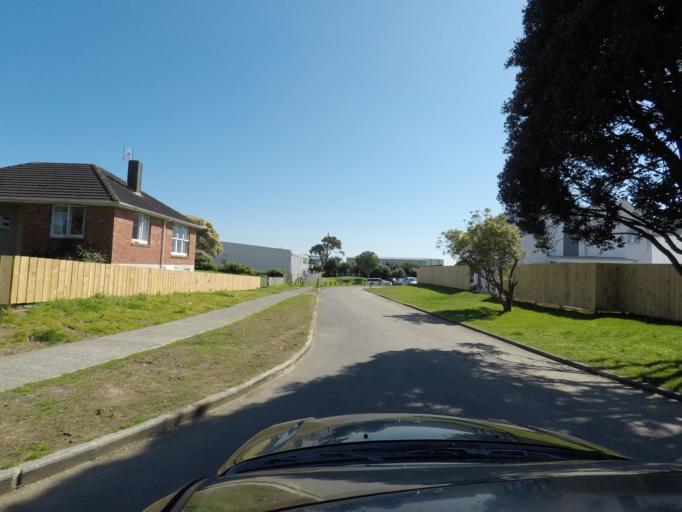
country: NZ
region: Auckland
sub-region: Auckland
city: Tamaki
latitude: -36.9243
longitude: 174.8585
